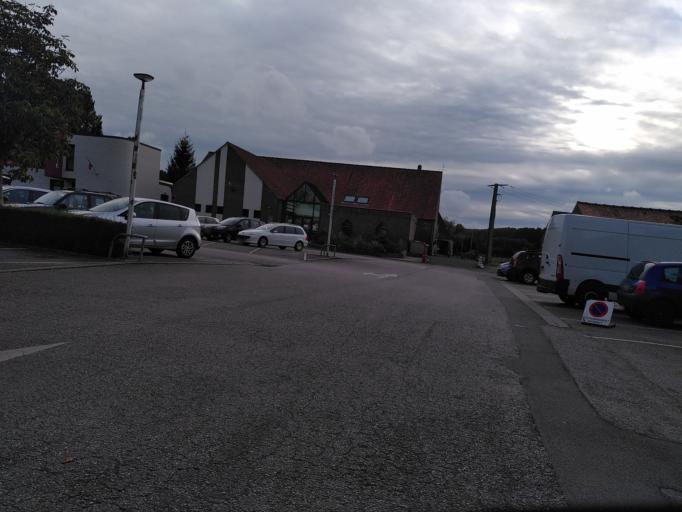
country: FR
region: Nord-Pas-de-Calais
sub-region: Departement du Pas-de-Calais
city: Therouanne
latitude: 50.6363
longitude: 2.2582
